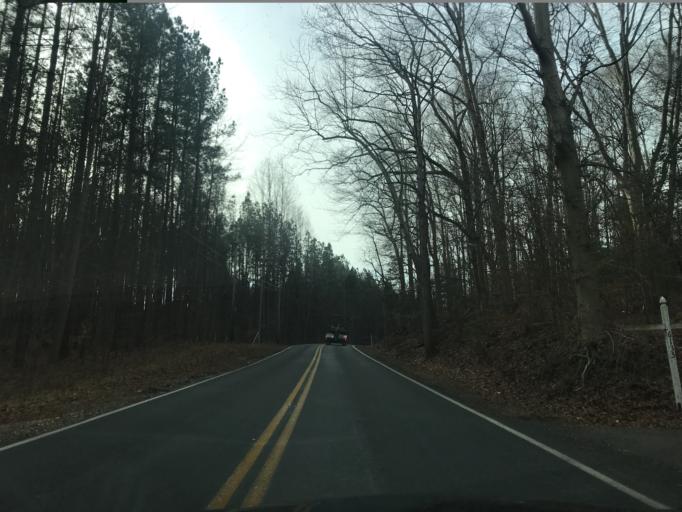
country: US
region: Maryland
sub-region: Charles County
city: Hughesville
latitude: 38.5440
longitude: -76.8409
